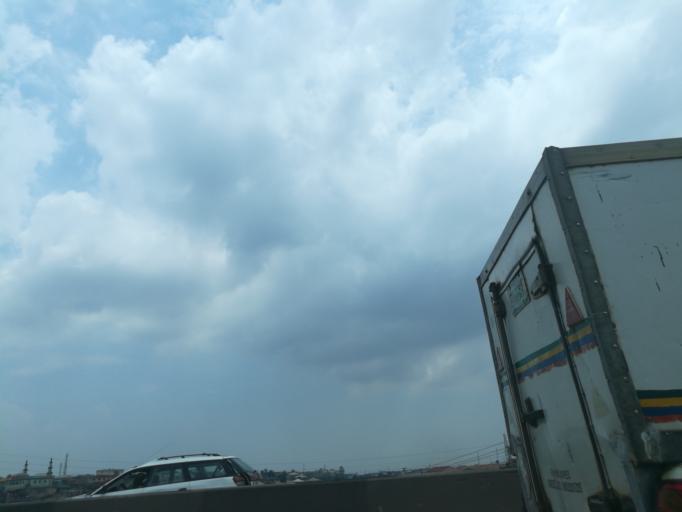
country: NG
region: Lagos
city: Ojota
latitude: 6.5799
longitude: 3.3730
